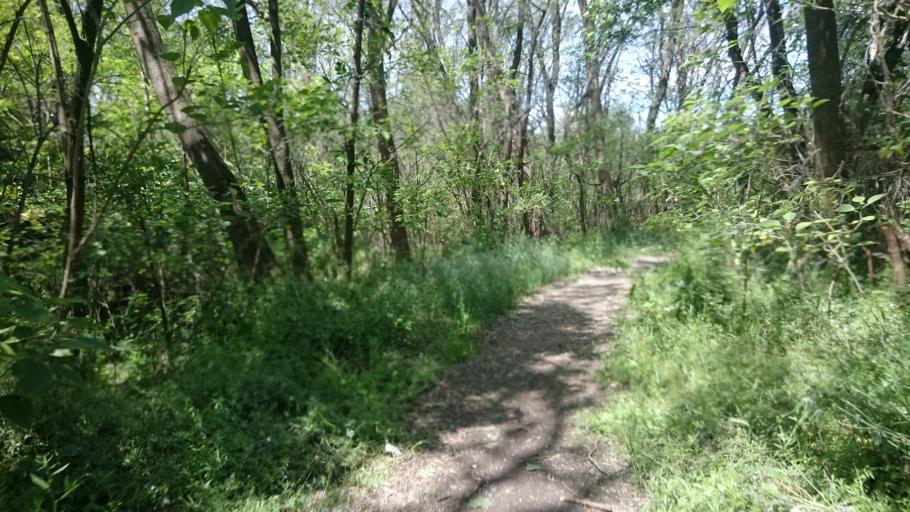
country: IT
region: Lombardy
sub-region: Provincia di Mantova
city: Mantova
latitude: 45.1439
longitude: 10.8061
